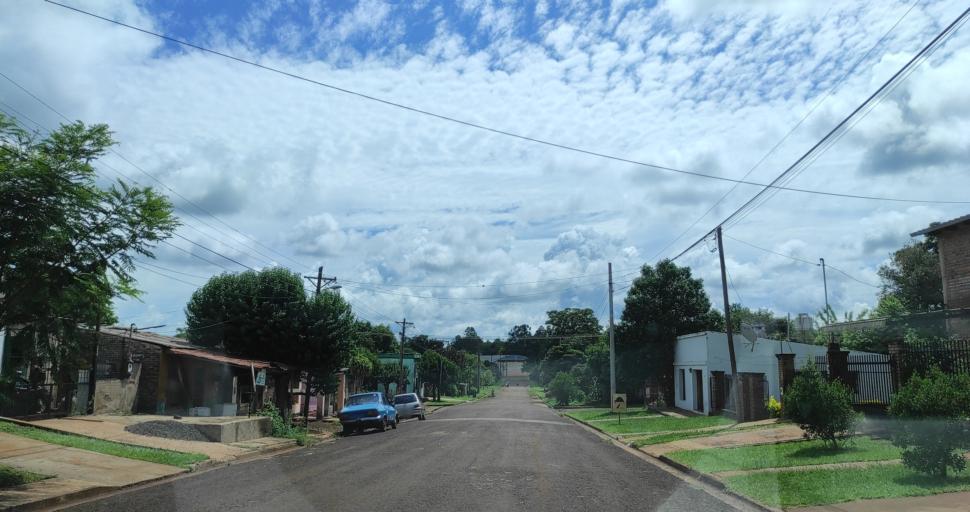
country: AR
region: Misiones
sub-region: Departamento de Apostoles
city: San Jose
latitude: -27.7682
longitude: -55.7762
